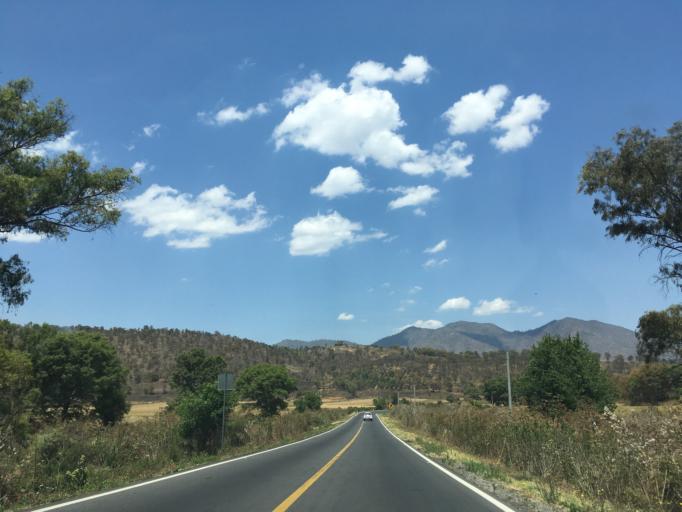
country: MX
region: Michoacan
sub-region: Chilchota
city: Tacuro (Santa Maria Tacuro)
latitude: 19.8352
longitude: -102.0326
